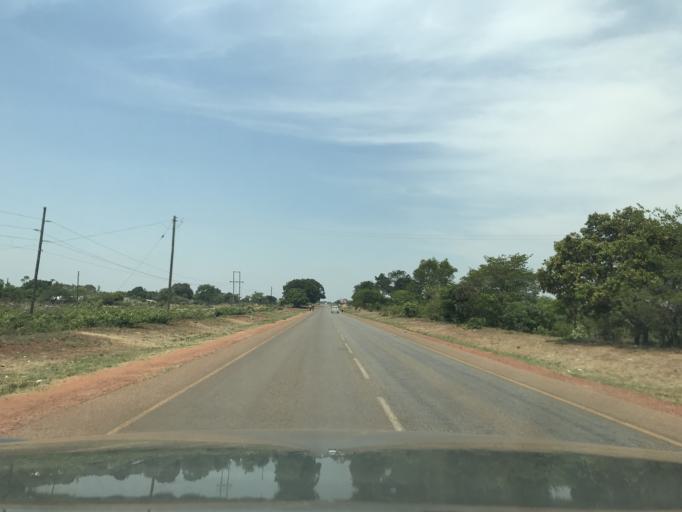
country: ZM
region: Northern
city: Kasama
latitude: -10.2160
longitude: 31.1487
